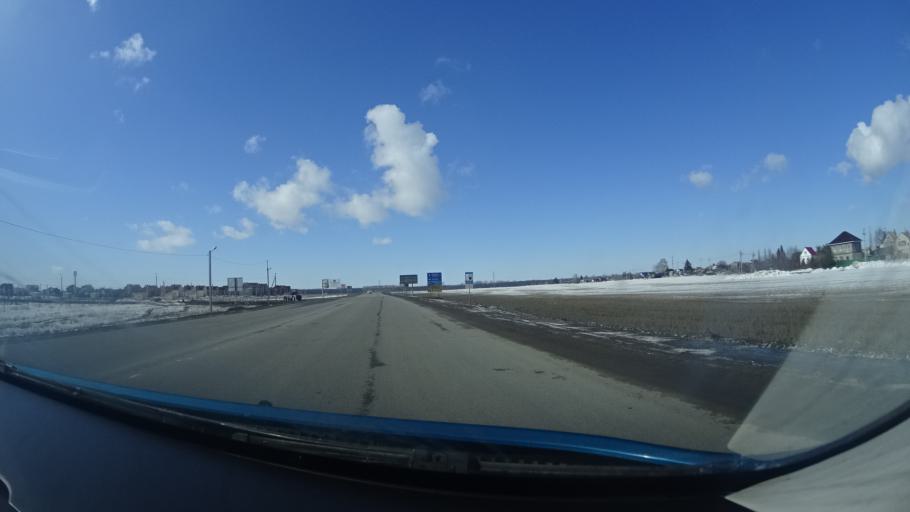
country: RU
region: Bashkortostan
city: Ufa
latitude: 54.6335
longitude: 55.9227
